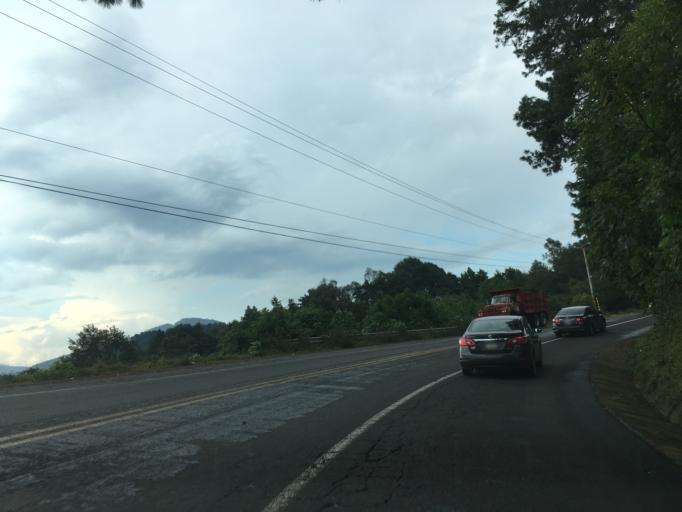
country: MX
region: Michoacan
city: Capacuaro
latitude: 19.5189
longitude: -102.0778
